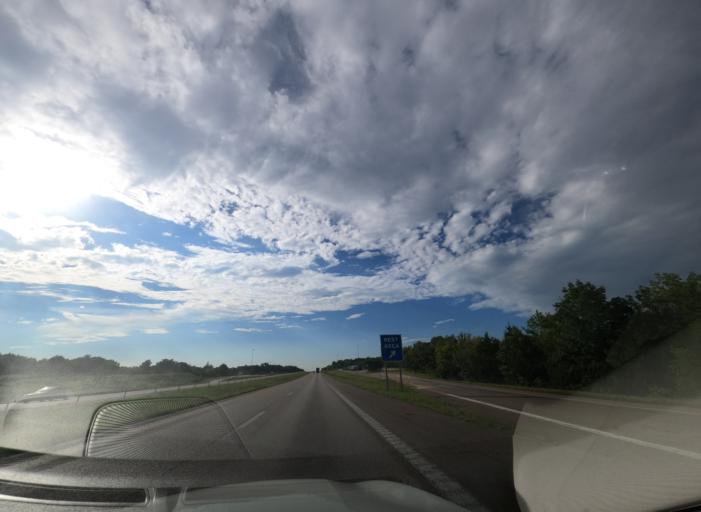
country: US
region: Missouri
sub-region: Sainte Genevieve County
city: Sainte Genevieve
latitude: 38.0289
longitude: -90.2460
